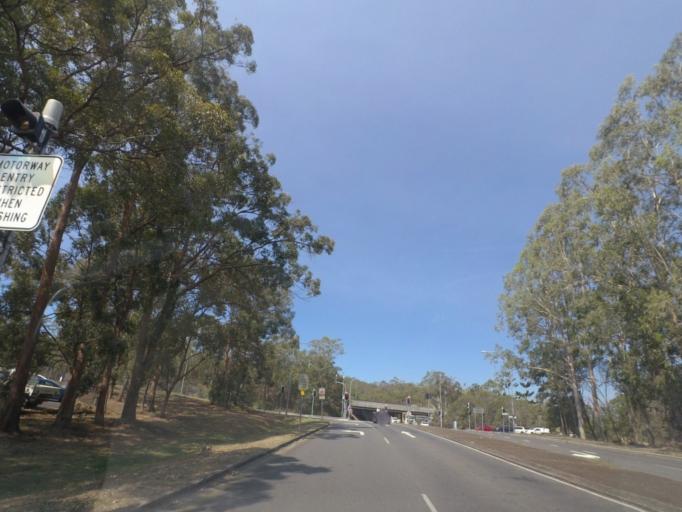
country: AU
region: Queensland
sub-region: Brisbane
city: Nathan
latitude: -27.5505
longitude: 153.0652
